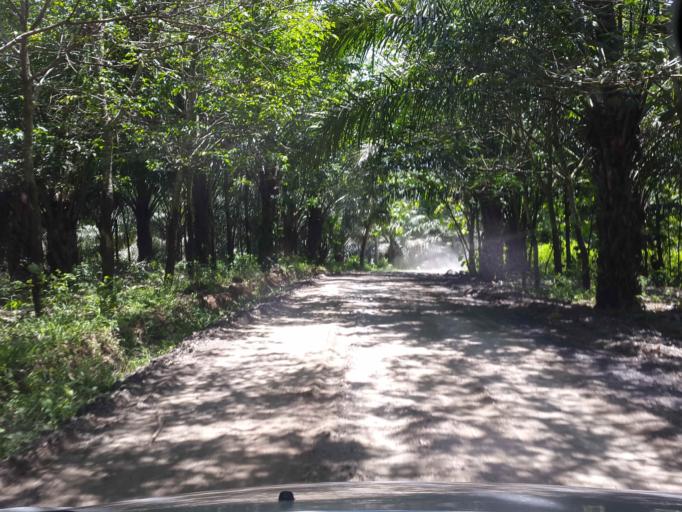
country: ID
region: Lampung
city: Panjang
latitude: -5.4933
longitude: 105.4336
